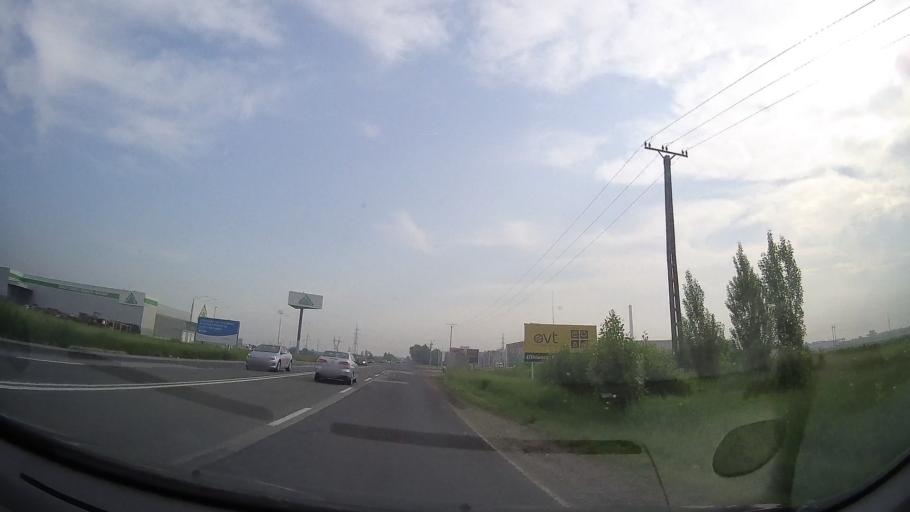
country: RO
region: Timis
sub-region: Comuna Giroc
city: Chisoda
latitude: 45.7021
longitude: 21.1835
